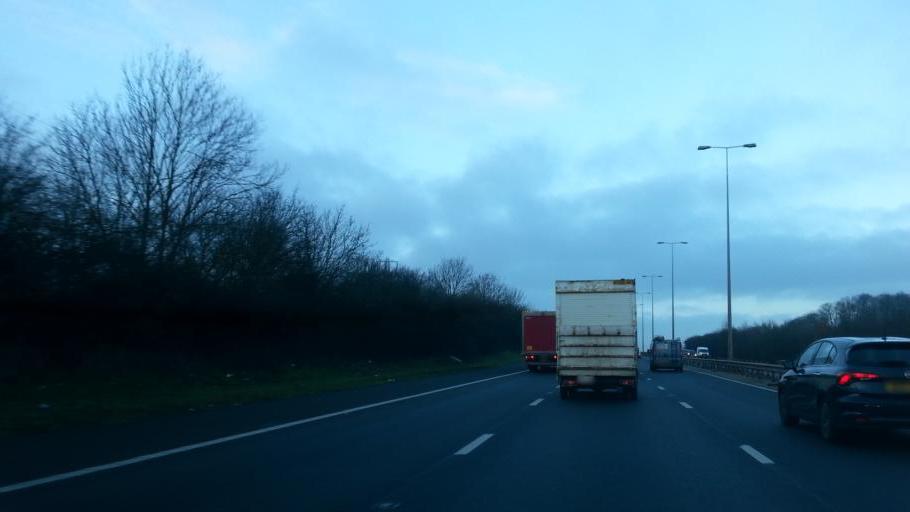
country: GB
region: England
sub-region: Worcestershire
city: Worcester
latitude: 52.1860
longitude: -2.1705
